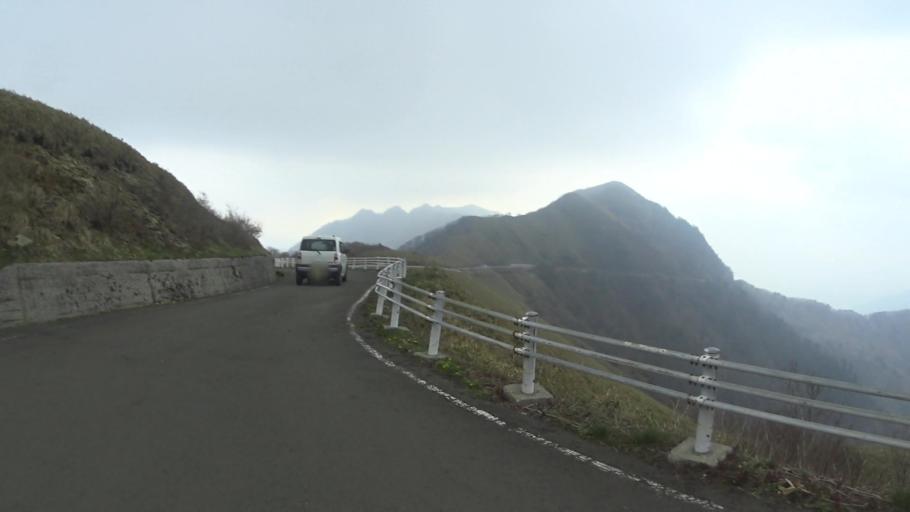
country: JP
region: Ehime
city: Saijo
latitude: 33.7824
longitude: 133.2254
